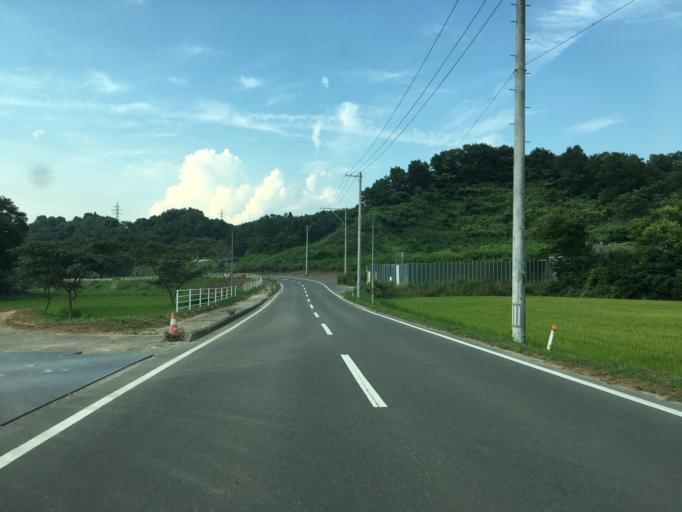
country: JP
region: Fukushima
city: Nihommatsu
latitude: 37.5466
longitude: 140.4417
